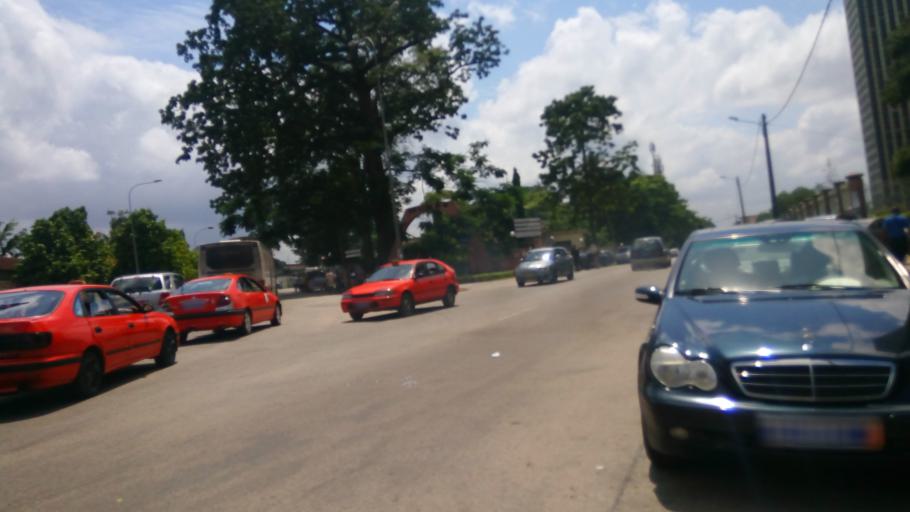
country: CI
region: Lagunes
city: Abidjan
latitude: 5.3325
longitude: -4.0238
